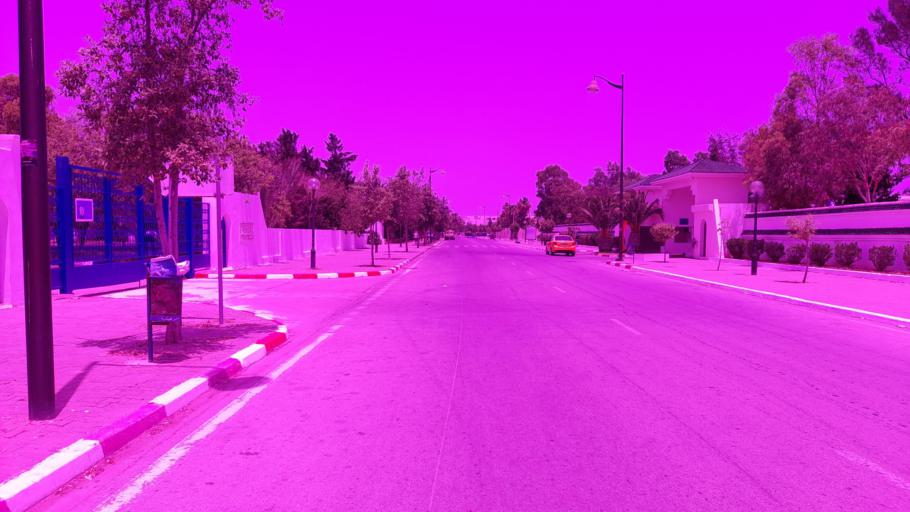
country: TN
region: Nabul
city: Al Hammamat
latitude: 36.3572
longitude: 10.5279
